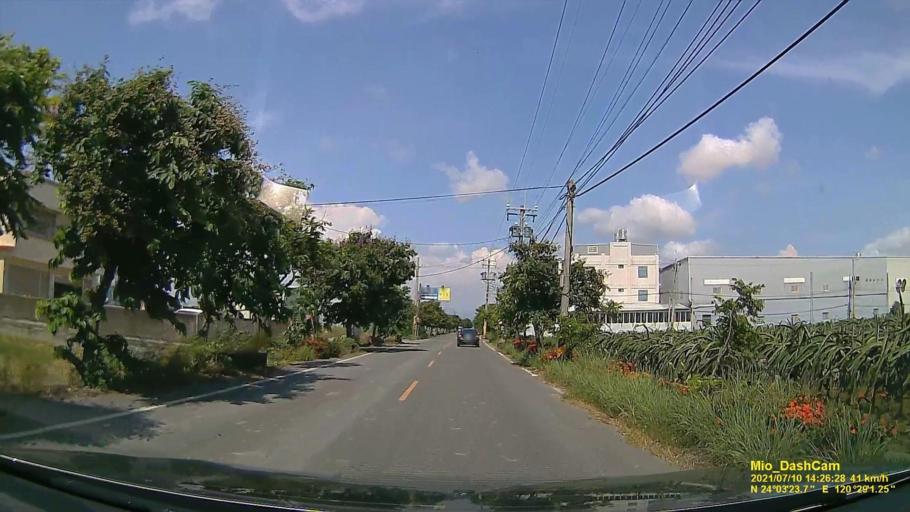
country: TW
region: Taiwan
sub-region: Changhua
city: Chang-hua
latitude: 24.0566
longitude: 120.4838
